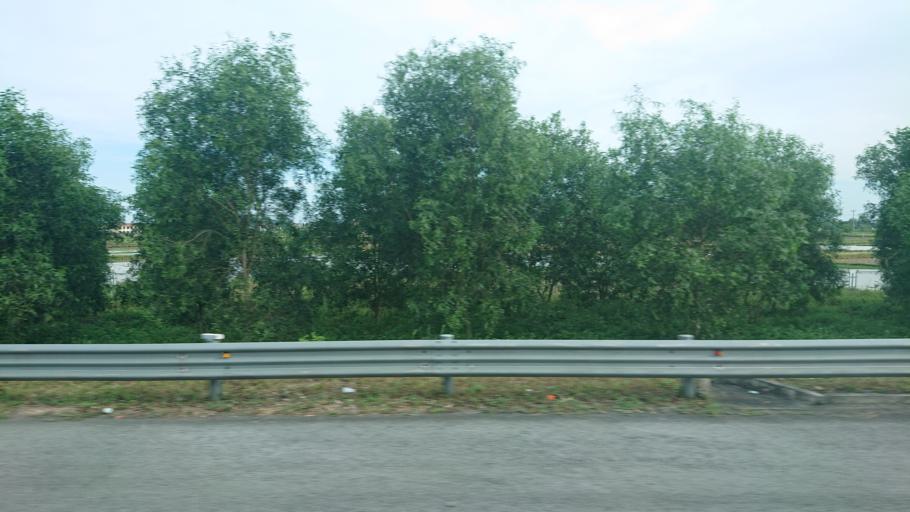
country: VN
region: Hai Phong
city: Nui Doi
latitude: 20.7656
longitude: 106.6524
